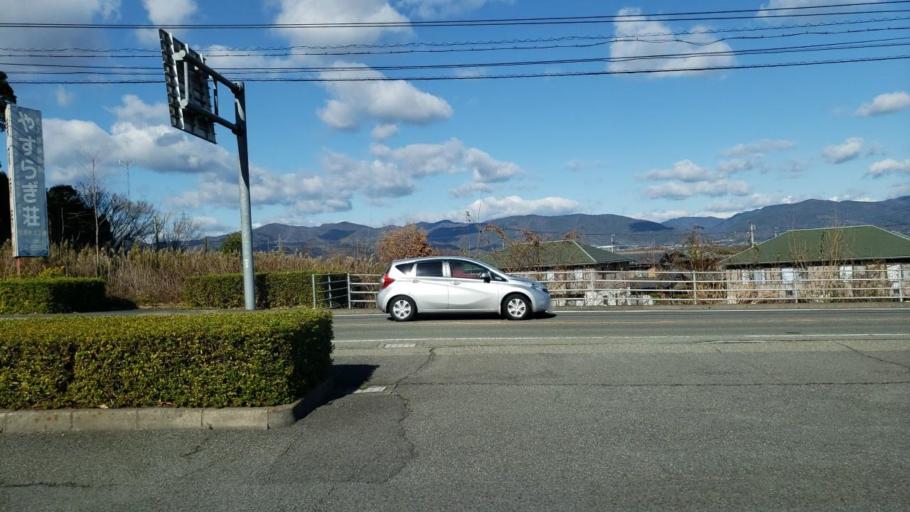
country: JP
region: Tokushima
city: Kamojimacho-jogejima
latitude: 34.0650
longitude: 134.3251
